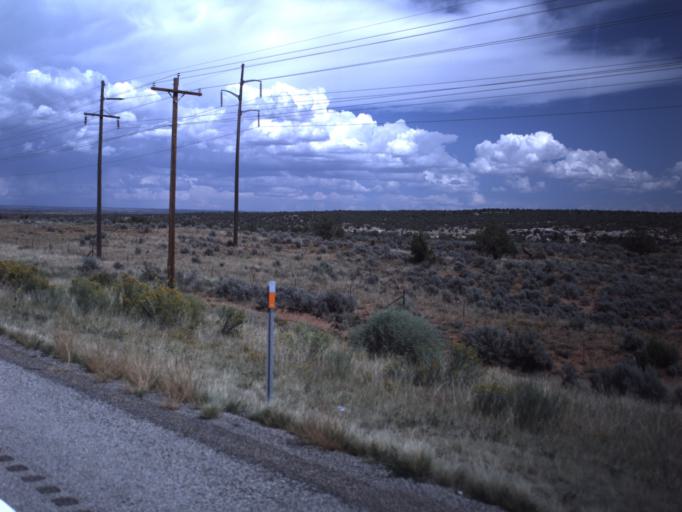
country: US
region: Utah
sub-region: San Juan County
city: Blanding
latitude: 37.5291
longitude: -109.4941
